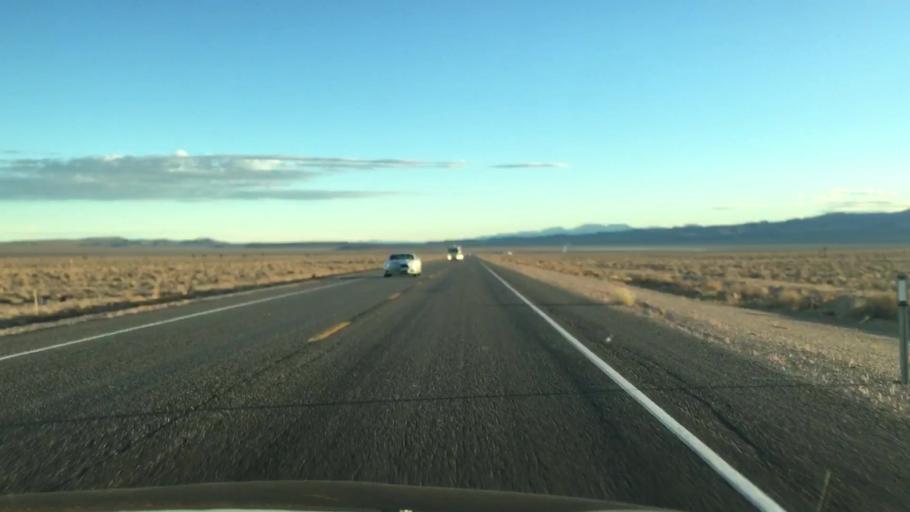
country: US
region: Nevada
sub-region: Esmeralda County
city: Goldfield
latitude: 37.5225
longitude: -117.1903
